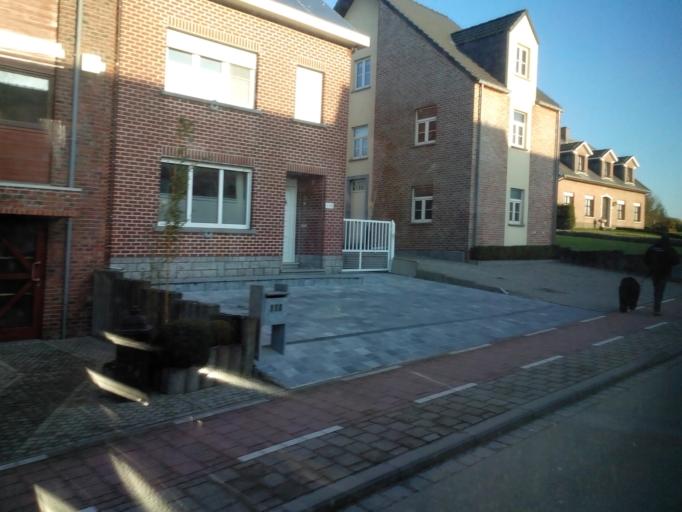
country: BE
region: Flanders
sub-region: Provincie Vlaams-Brabant
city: Bierbeek
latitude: 50.8418
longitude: 4.7297
